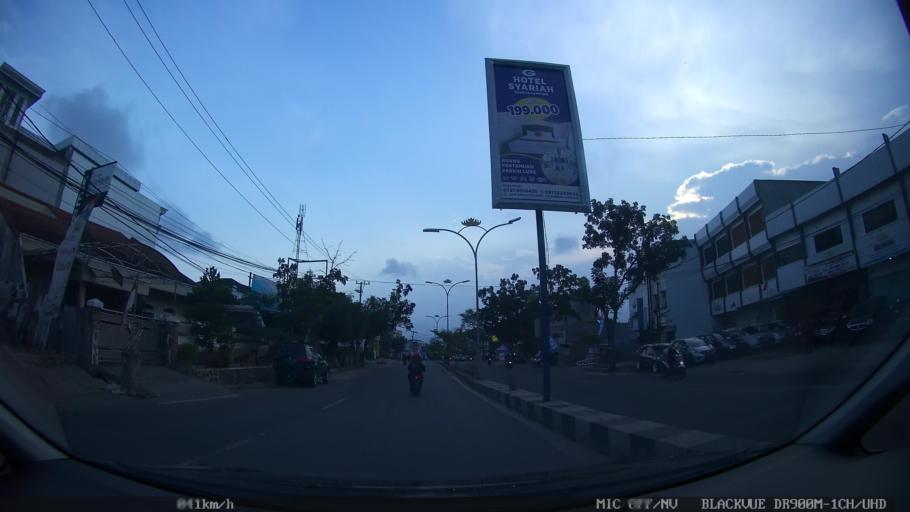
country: ID
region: Lampung
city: Kedaton
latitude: -5.3991
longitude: 105.2882
